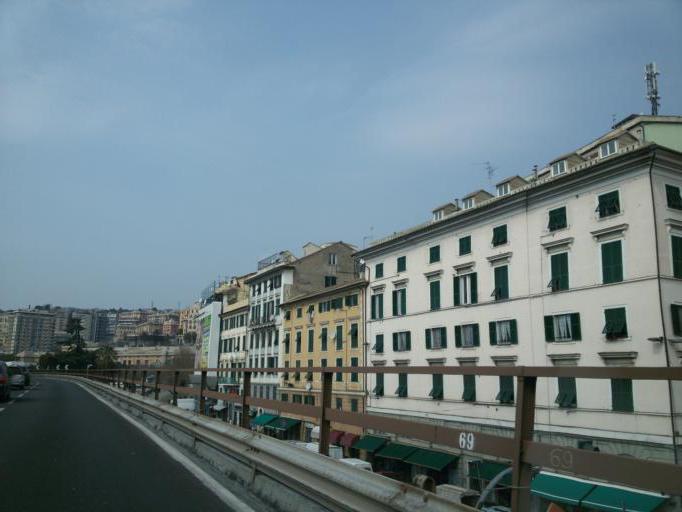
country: IT
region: Liguria
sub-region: Provincia di Genova
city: San Teodoro
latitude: 44.4154
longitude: 8.9220
